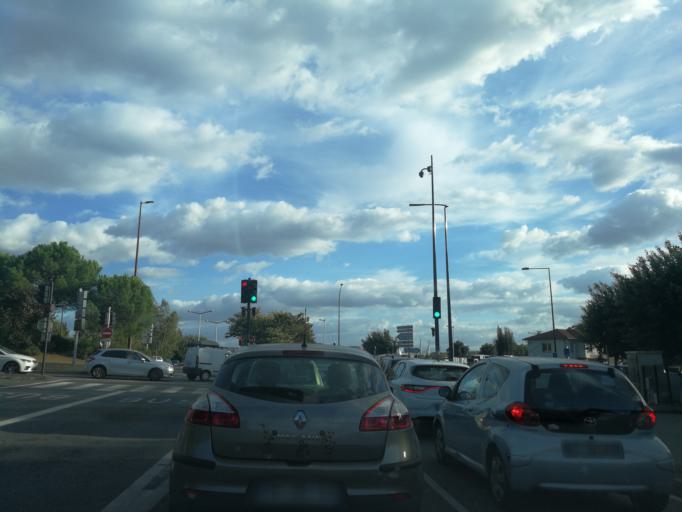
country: FR
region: Midi-Pyrenees
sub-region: Departement de la Haute-Garonne
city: Balma
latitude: 43.6274
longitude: 1.4772
